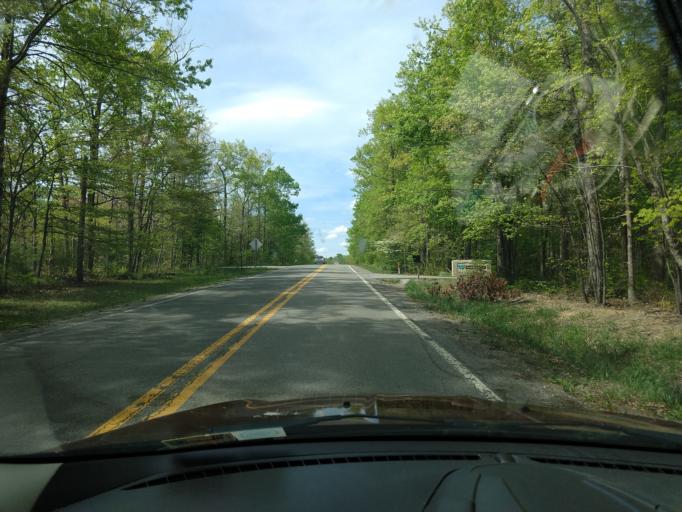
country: US
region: West Virginia
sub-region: Raleigh County
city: Daniels
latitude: 37.7857
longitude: -81.1162
